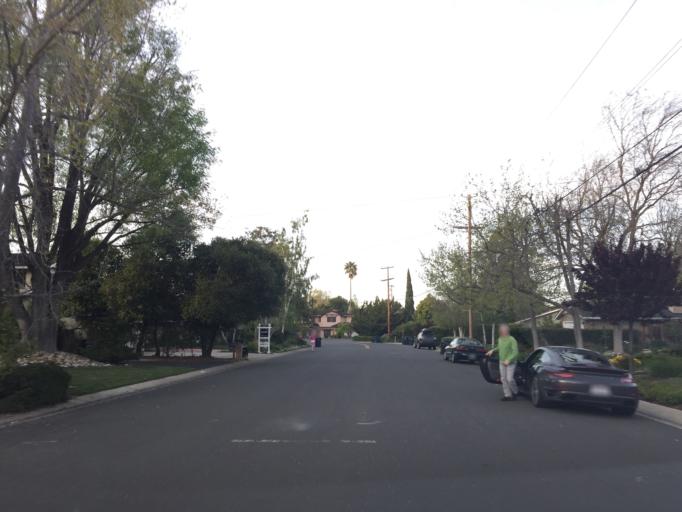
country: US
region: California
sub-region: Santa Clara County
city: Los Altos
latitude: 37.3907
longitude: -122.1109
